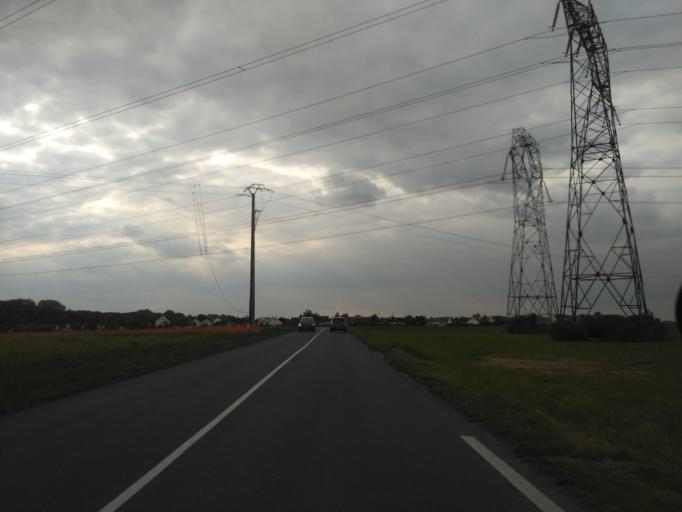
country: FR
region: Ile-de-France
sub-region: Departement de Seine-et-Marne
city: Voisenon
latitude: 48.5687
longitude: 2.6742
